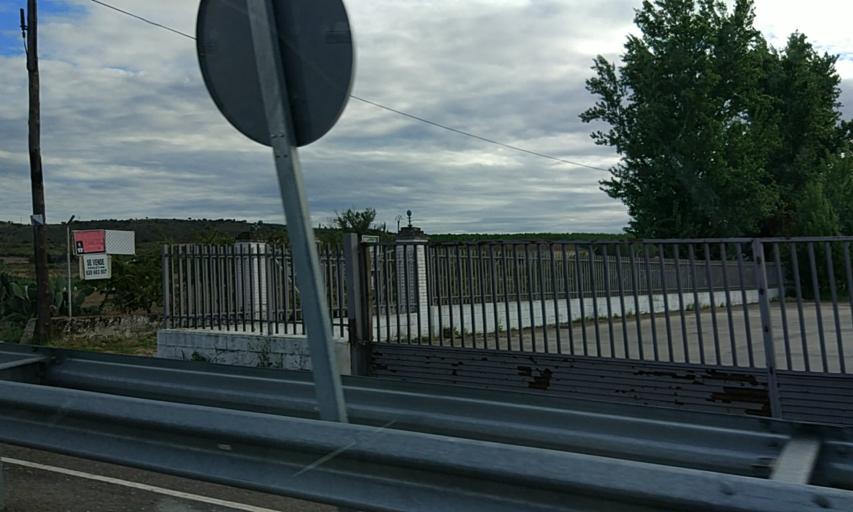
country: ES
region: Extremadura
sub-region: Provincia de Caceres
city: Coria
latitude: 39.9682
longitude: -6.5206
